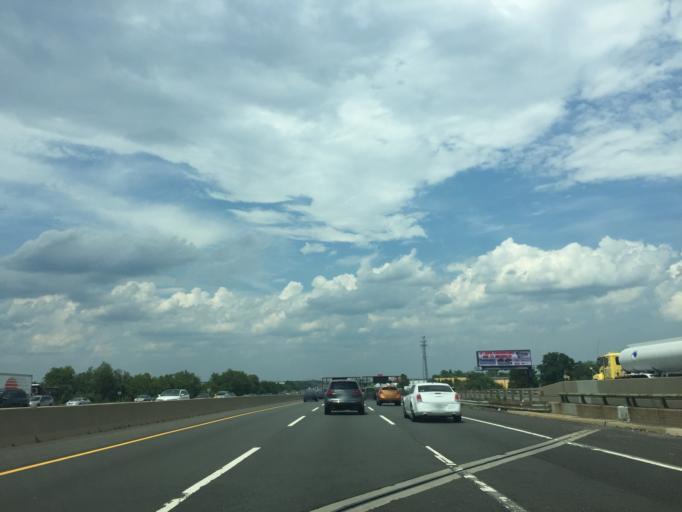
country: US
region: New Jersey
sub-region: Middlesex County
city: Rossmoor
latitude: 40.3582
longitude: -74.4700
